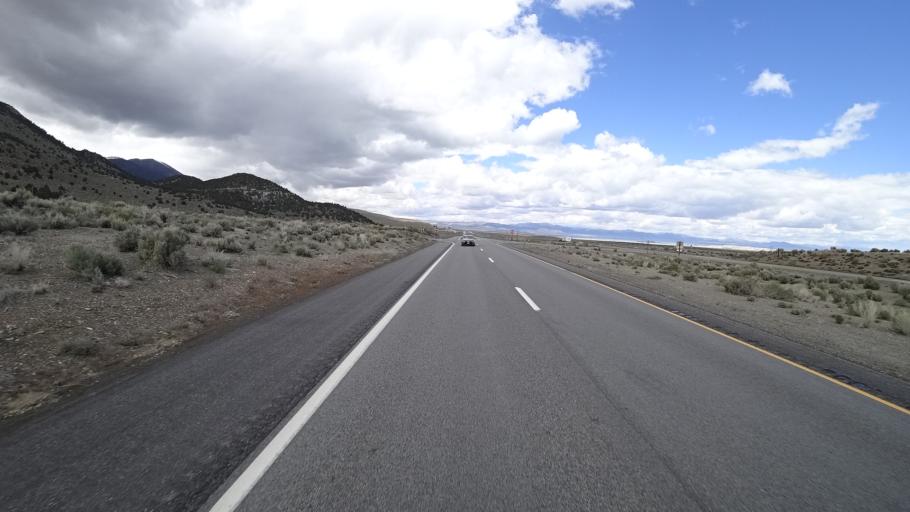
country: US
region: California
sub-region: Mono County
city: Mammoth Lakes
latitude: 37.9170
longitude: -119.0972
